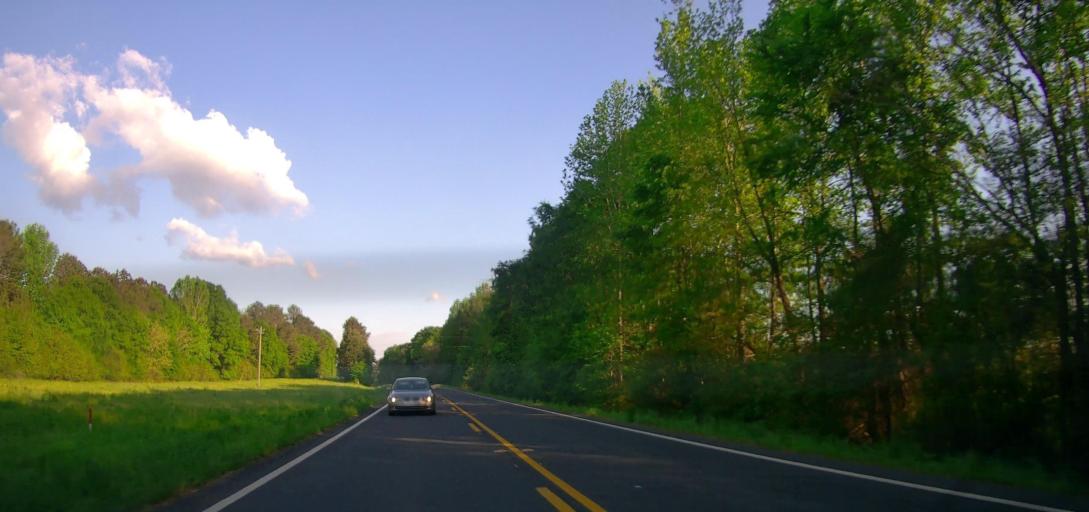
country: US
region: Georgia
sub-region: Jasper County
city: Monticello
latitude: 33.4103
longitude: -83.6041
